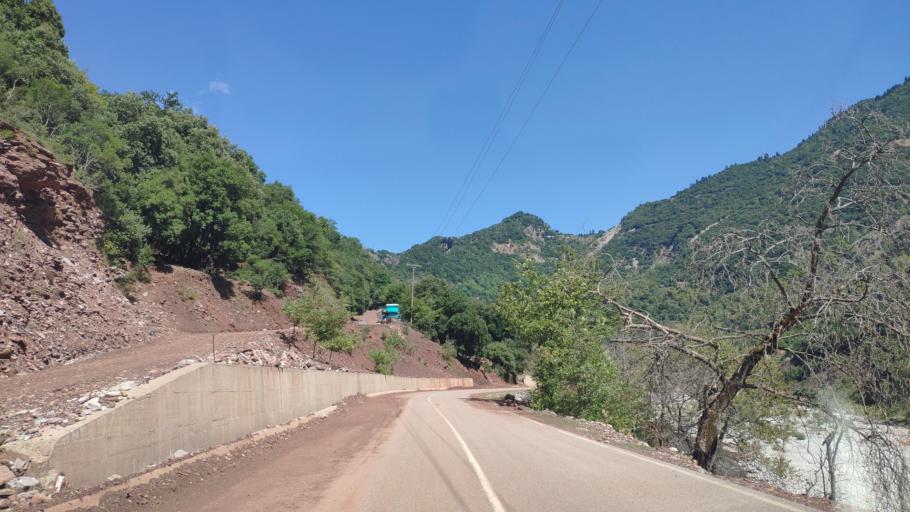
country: GR
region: Central Greece
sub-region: Nomos Evrytanias
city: Kerasochori
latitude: 39.0626
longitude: 21.6067
